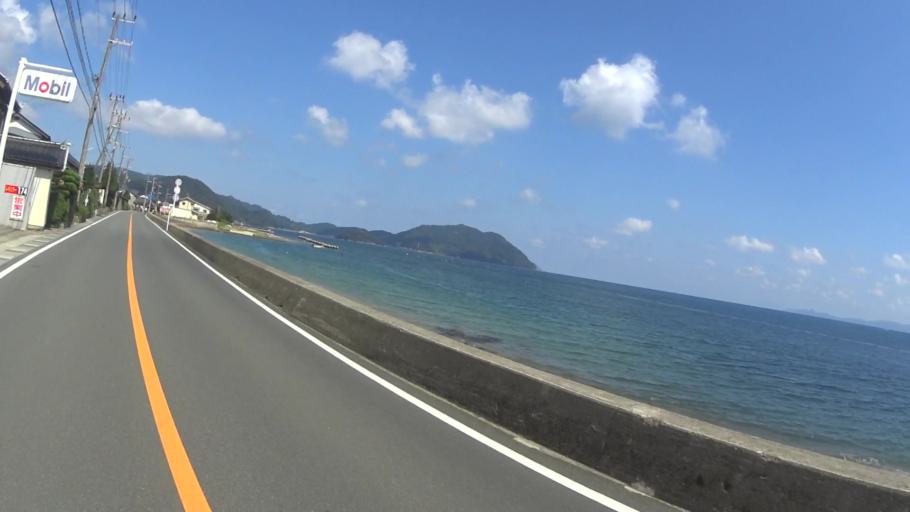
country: JP
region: Kyoto
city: Miyazu
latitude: 35.6536
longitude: 135.2565
